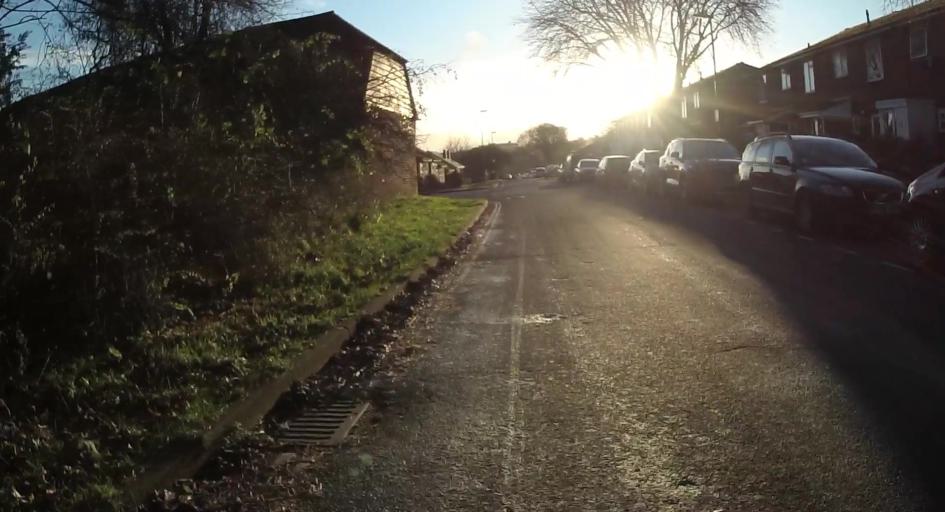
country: GB
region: England
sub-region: Hampshire
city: Winchester
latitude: 51.0741
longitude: -1.3107
